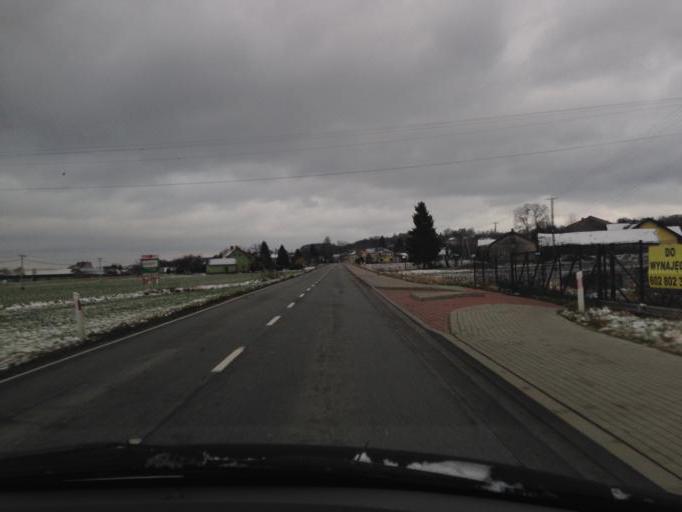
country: PL
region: Lesser Poland Voivodeship
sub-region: Powiat tarnowski
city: Zakliczyn
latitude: 49.8514
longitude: 20.8339
